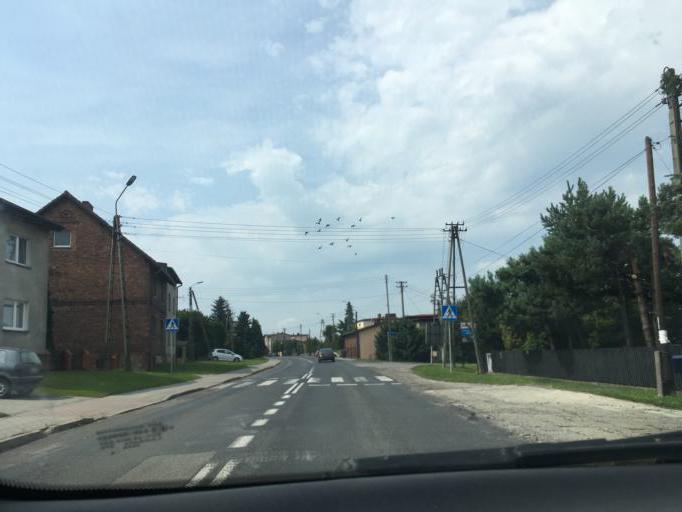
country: PL
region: Silesian Voivodeship
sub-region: Powiat rybnicki
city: Belk
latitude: 50.1305
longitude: 18.7165
